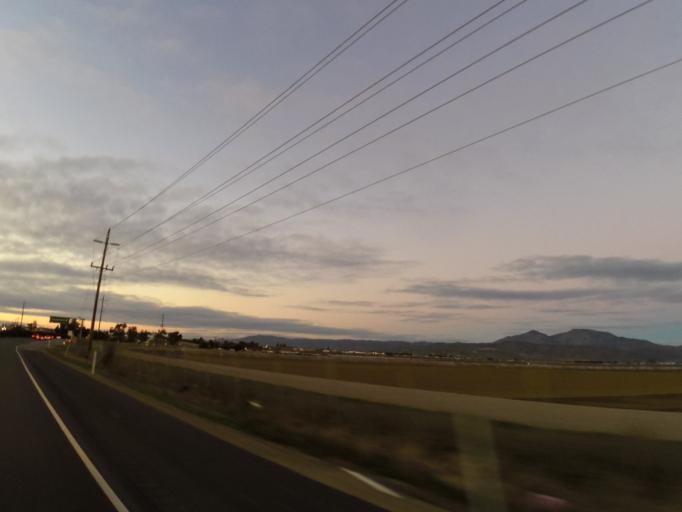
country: US
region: California
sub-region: Monterey County
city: Greenfield
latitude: 36.3097
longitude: -121.2304
